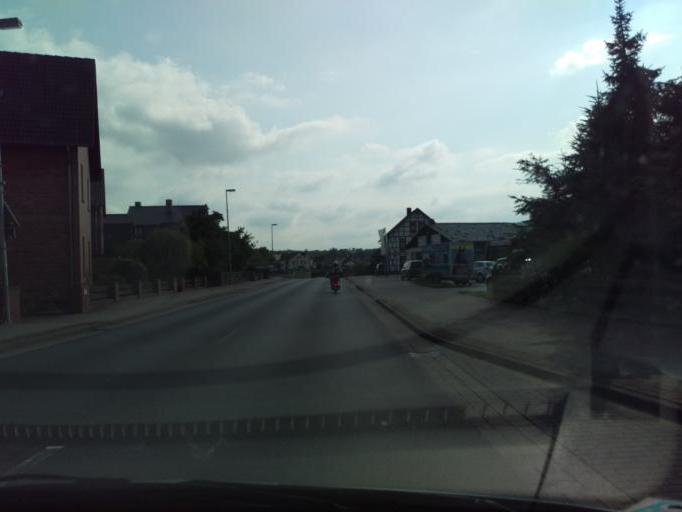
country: DE
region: Lower Saxony
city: Arpke
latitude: 52.3564
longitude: 10.1157
